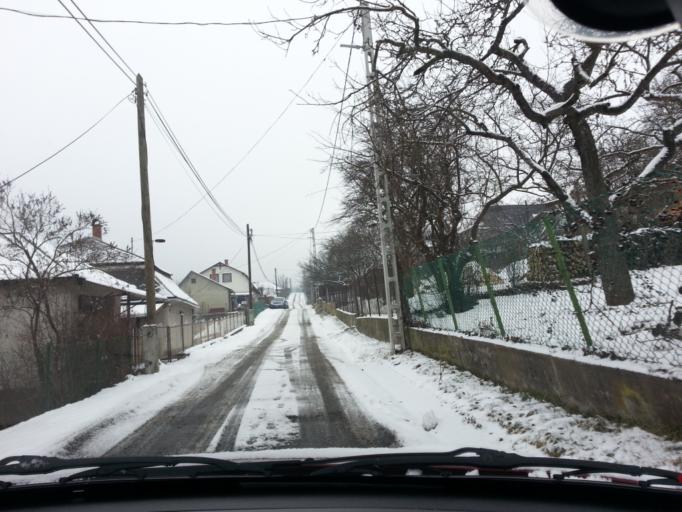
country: HU
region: Nograd
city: Somoskoujfalu
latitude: 48.1280
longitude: 19.8794
